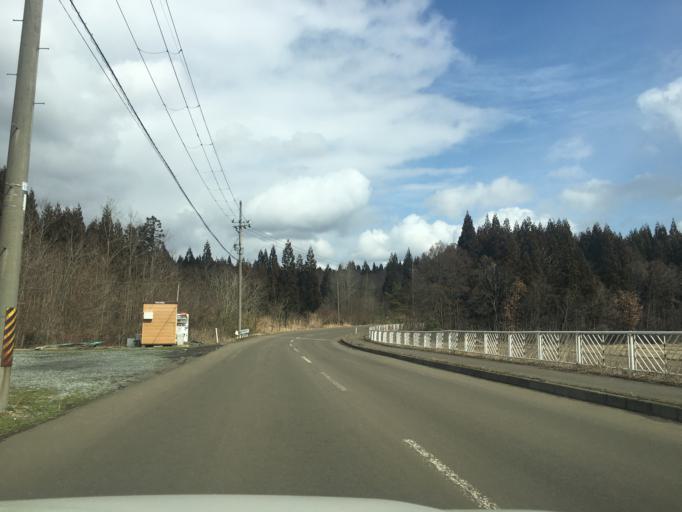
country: JP
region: Akita
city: Takanosu
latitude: 40.1887
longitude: 140.3434
